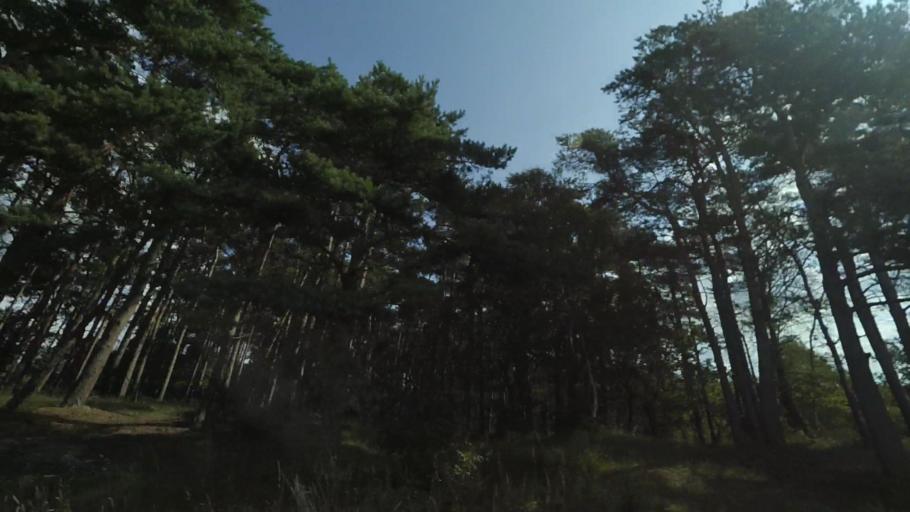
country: DK
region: Central Jutland
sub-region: Norddjurs Kommune
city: Allingabro
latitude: 56.5129
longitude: 10.3943
